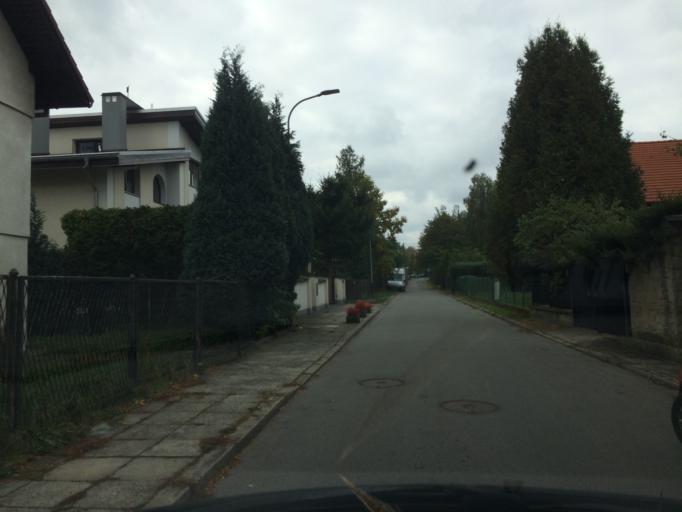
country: PL
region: Lesser Poland Voivodeship
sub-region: Powiat wielicki
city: Czarnochowice
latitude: 50.0125
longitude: 20.0289
